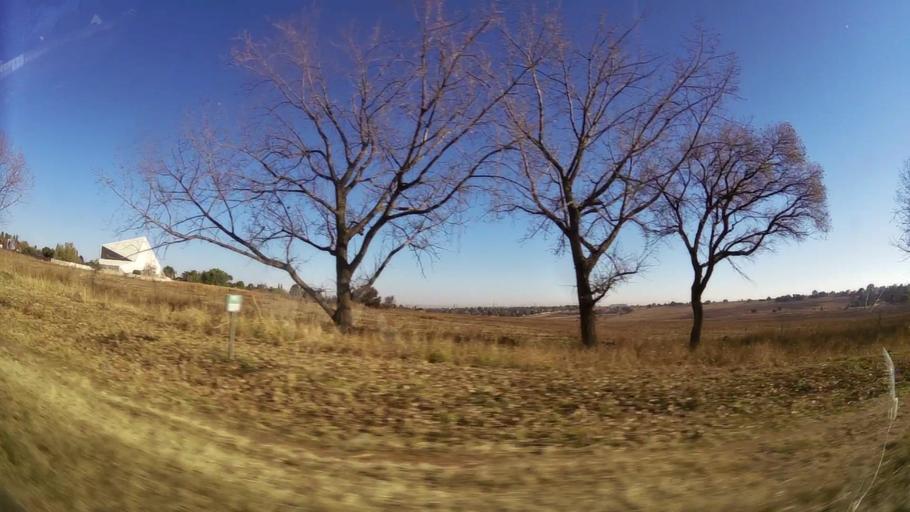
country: ZA
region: Gauteng
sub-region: Ekurhuleni Metropolitan Municipality
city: Tembisa
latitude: -26.0459
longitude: 28.2436
